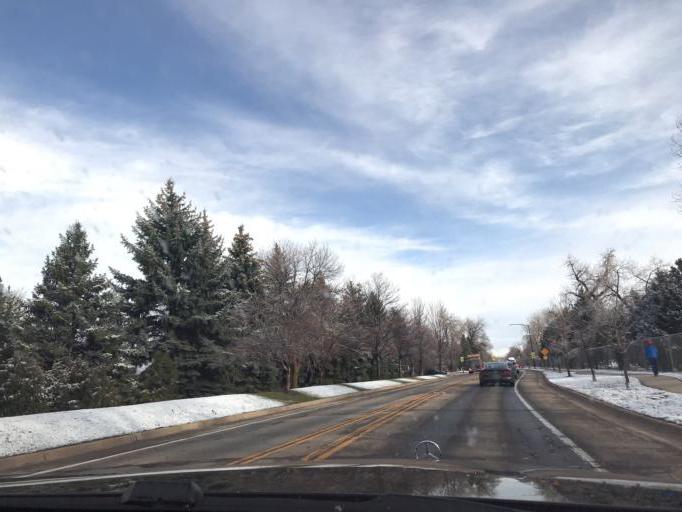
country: US
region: Colorado
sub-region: Boulder County
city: Boulder
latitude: 40.0083
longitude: -105.2253
